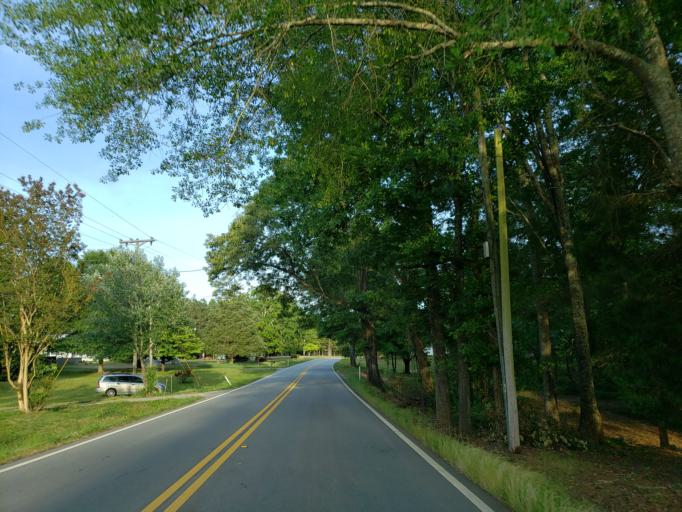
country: US
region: Georgia
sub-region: Carroll County
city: Mount Zion
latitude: 33.6081
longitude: -85.1489
